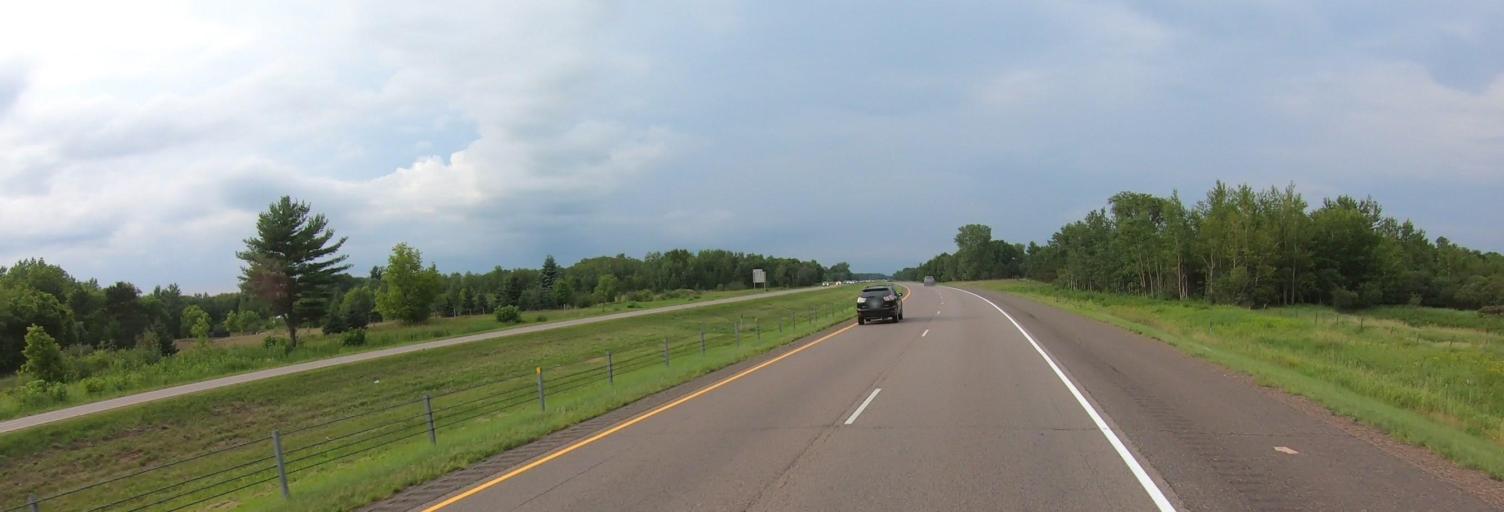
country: US
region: Minnesota
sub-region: Chisago County
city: Stacy
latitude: 45.4133
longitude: -92.9886
